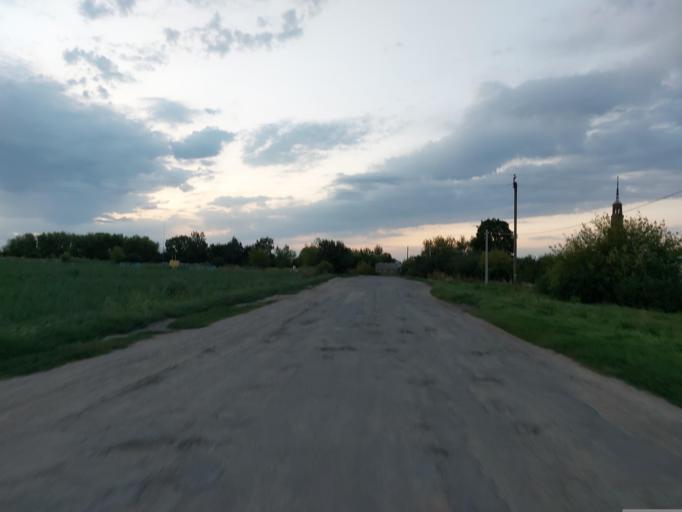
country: RU
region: Lipetsk
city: Dolgorukovo
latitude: 52.3749
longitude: 38.0524
